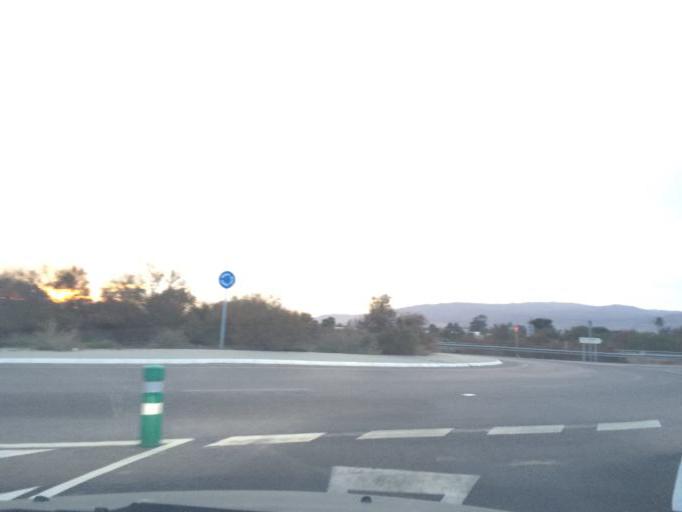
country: ES
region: Andalusia
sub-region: Provincia de Almeria
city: Almeria
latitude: 36.8324
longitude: -2.4032
